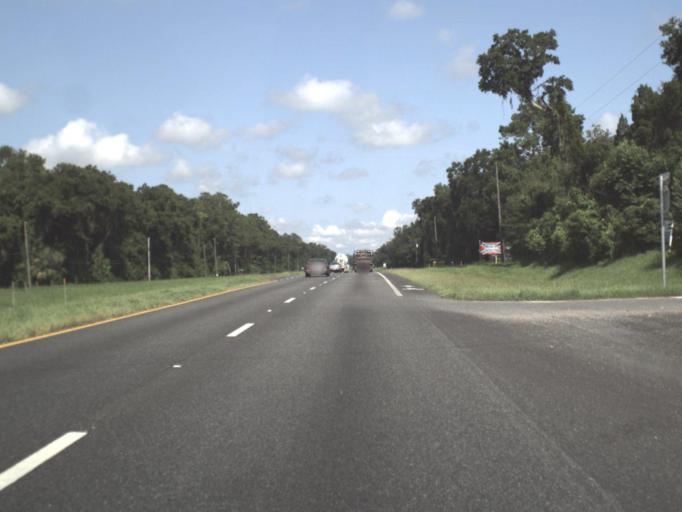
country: US
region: Florida
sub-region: Hernando County
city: Hill 'n Dale
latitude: 28.5306
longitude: -82.3255
